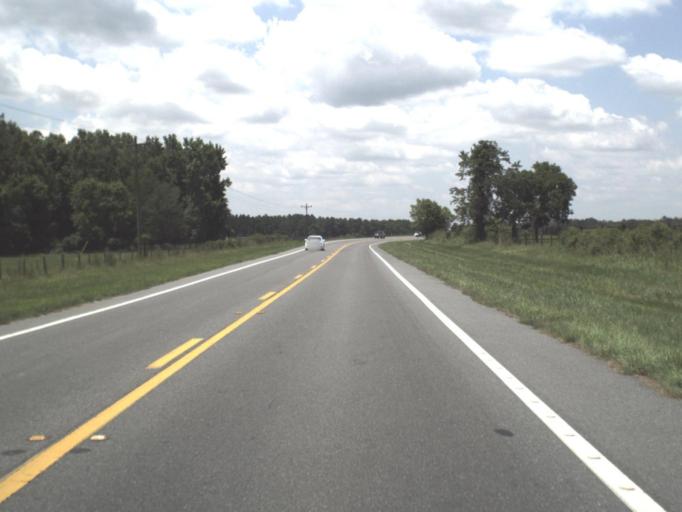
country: US
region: Florida
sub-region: Levy County
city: Williston
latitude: 29.4616
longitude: -82.4137
